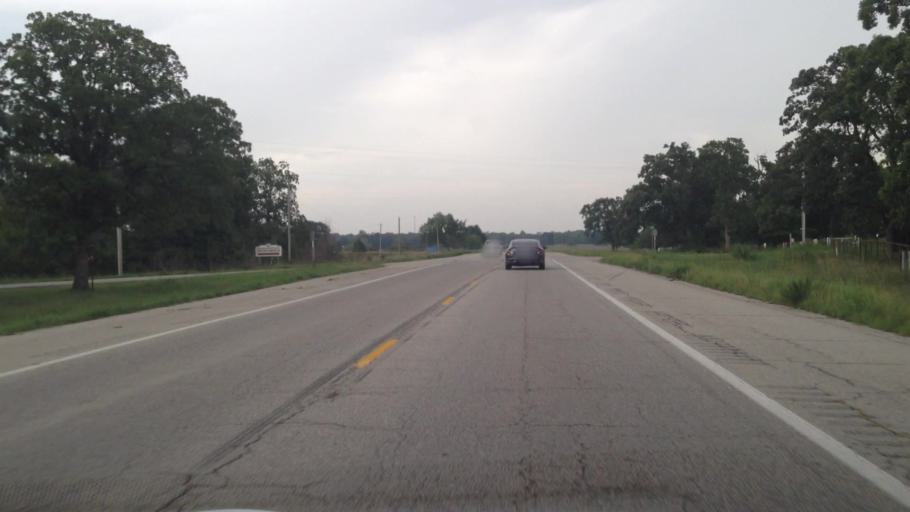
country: US
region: Kansas
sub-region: Cherokee County
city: Galena
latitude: 37.0144
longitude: -94.6316
